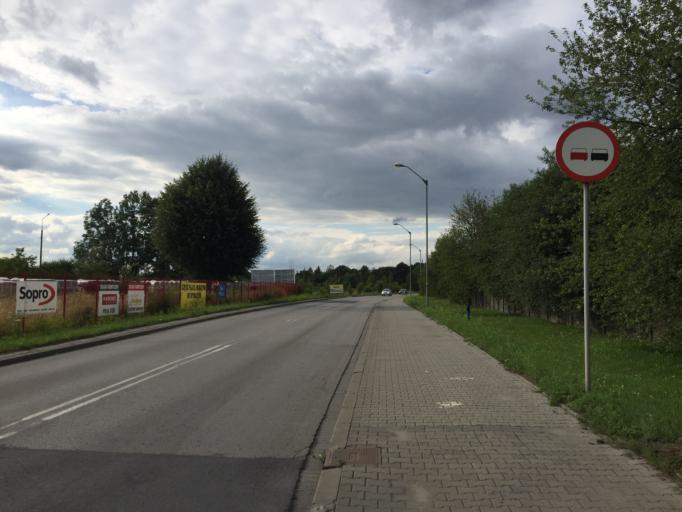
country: PL
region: Lesser Poland Voivodeship
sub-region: Powiat oswiecimski
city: Brzezinka
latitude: 50.0327
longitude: 19.1936
